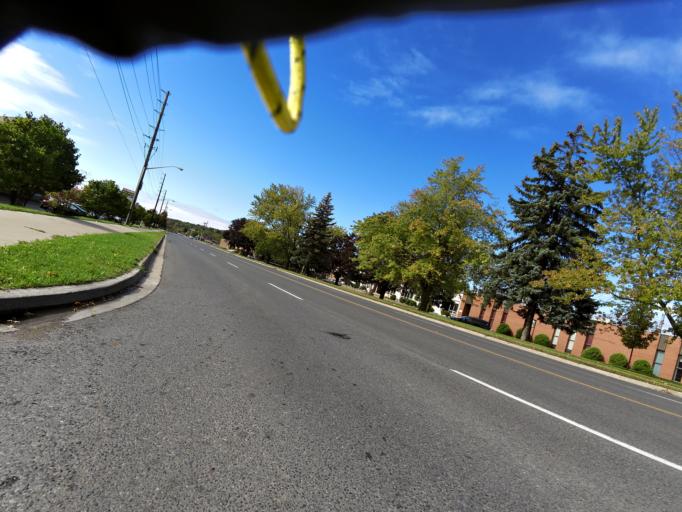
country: CA
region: Ontario
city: Cobourg
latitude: 43.9506
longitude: -78.2808
